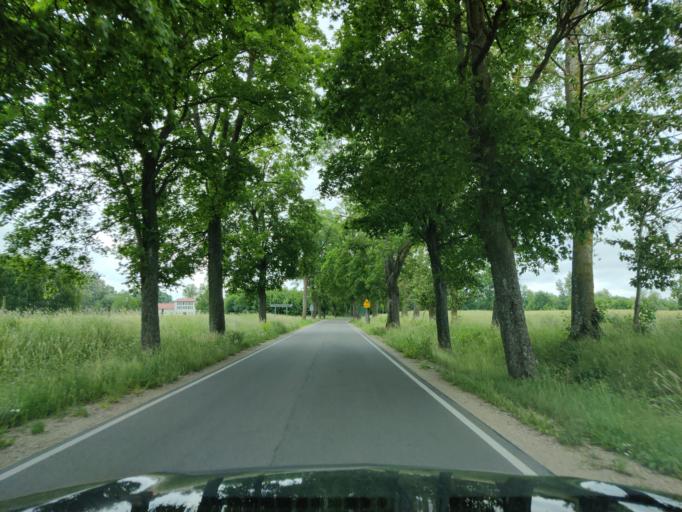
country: PL
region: Warmian-Masurian Voivodeship
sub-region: Powiat mragowski
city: Mikolajki
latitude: 53.8550
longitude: 21.6128
